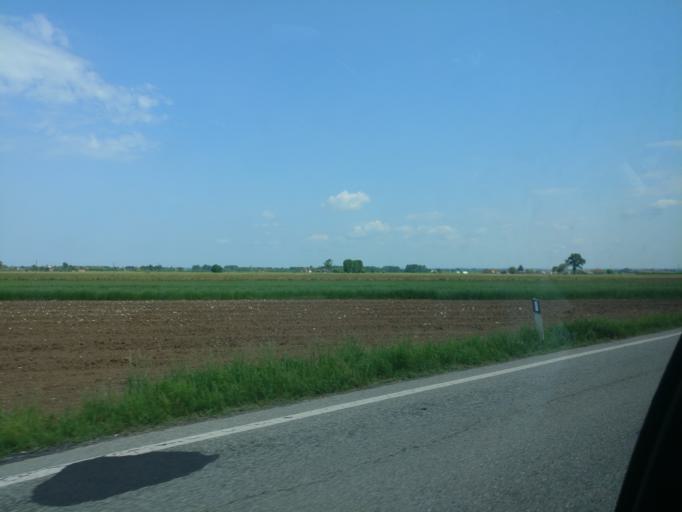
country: IT
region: Piedmont
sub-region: Provincia di Torino
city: Cavour
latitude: 44.7694
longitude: 7.3923
